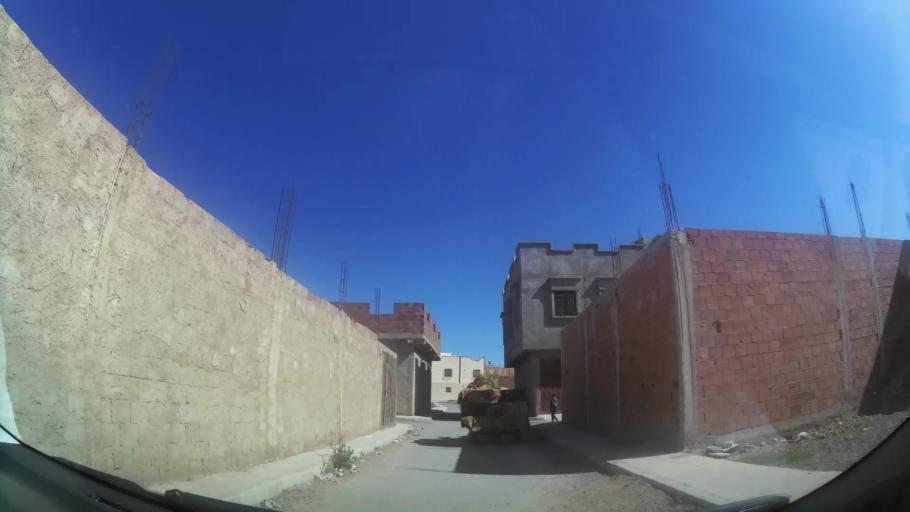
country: MA
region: Oriental
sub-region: Oujda-Angad
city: Oujda
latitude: 34.7230
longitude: -1.9022
